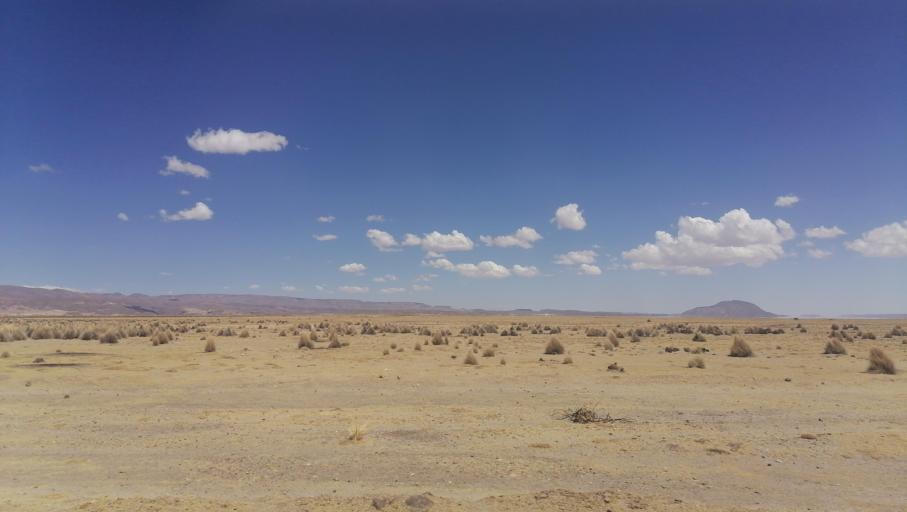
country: BO
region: Oruro
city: Challapata
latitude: -19.1720
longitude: -66.7992
